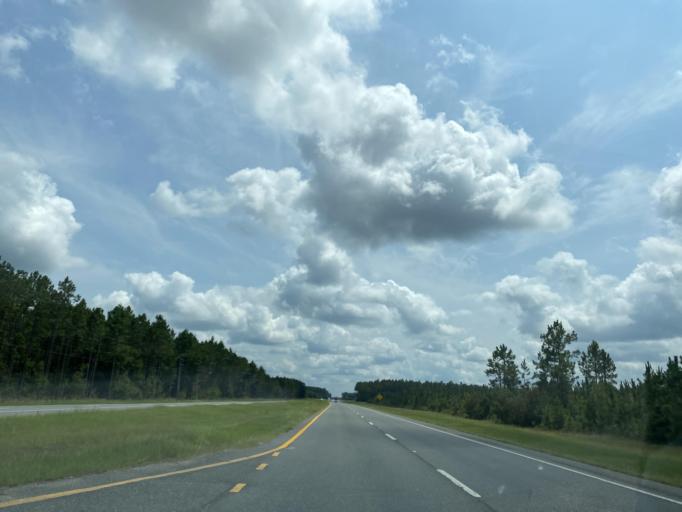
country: US
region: Georgia
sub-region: Ware County
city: Deenwood
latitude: 31.3592
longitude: -82.4637
